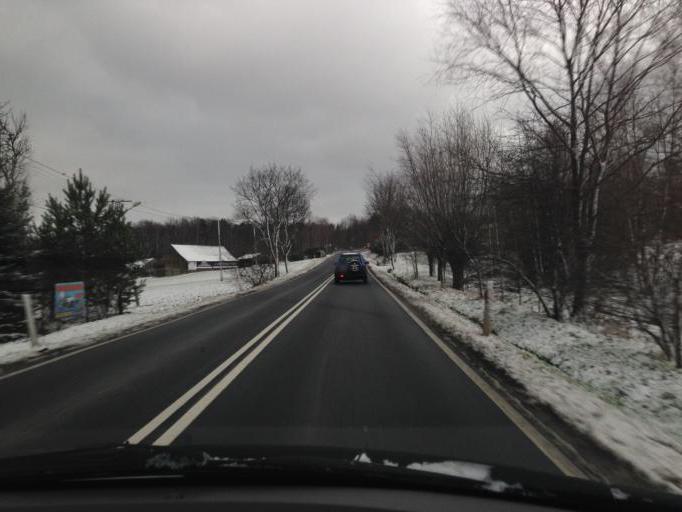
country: PL
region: Lesser Poland Voivodeship
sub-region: Powiat tarnowski
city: Siemiechow
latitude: 49.8486
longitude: 20.9301
